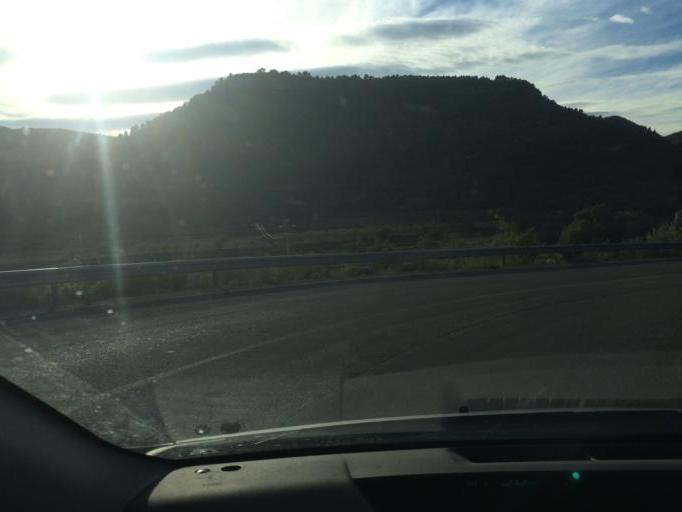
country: ES
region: Aragon
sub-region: Provincia de Huesca
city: Capella
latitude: 42.2849
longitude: 0.3569
